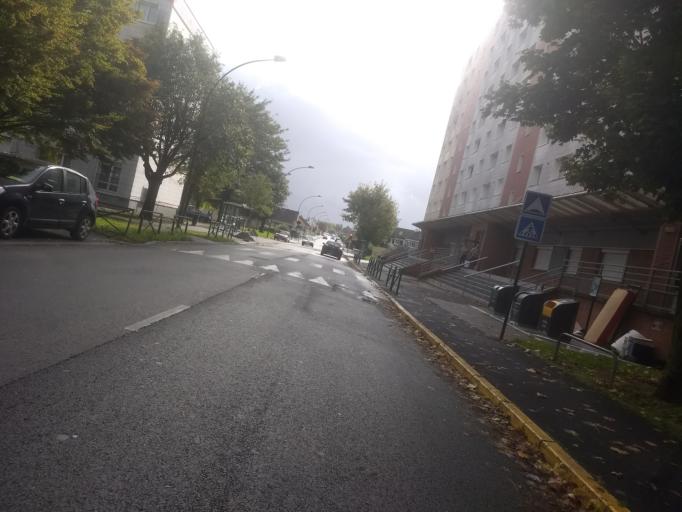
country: FR
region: Nord-Pas-de-Calais
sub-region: Departement du Pas-de-Calais
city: Achicourt
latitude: 50.2718
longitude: 2.7685
